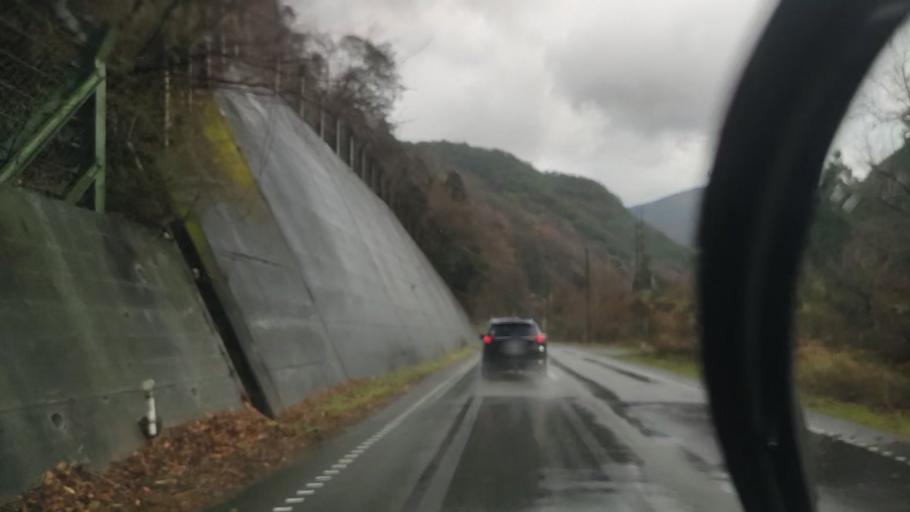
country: JP
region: Tokushima
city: Kamojimacho-jogejima
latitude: 34.1658
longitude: 134.3434
